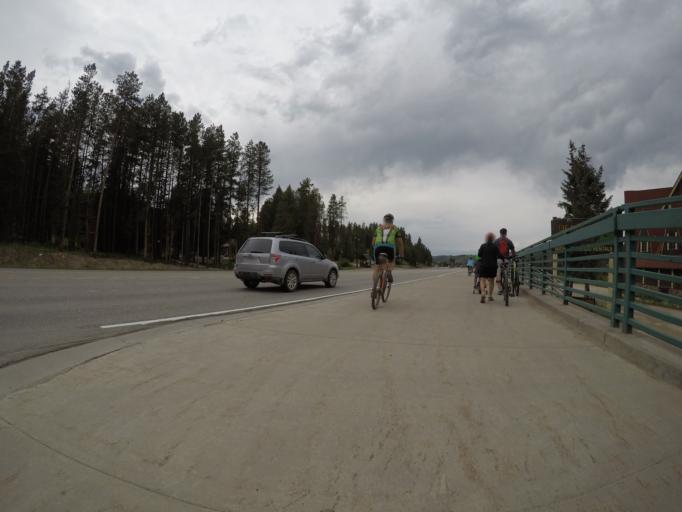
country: US
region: Colorado
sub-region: Grand County
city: Fraser
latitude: 39.9128
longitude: -105.7820
